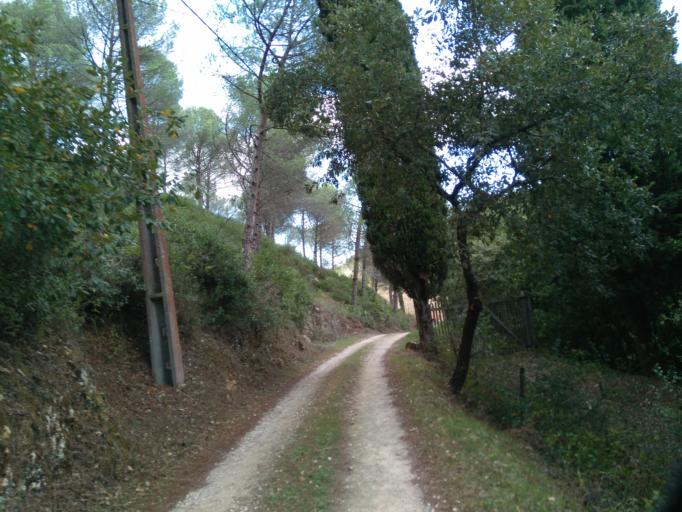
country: PT
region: Leiria
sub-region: Porto de Mos
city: Porto de Mos
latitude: 39.5927
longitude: -8.8101
